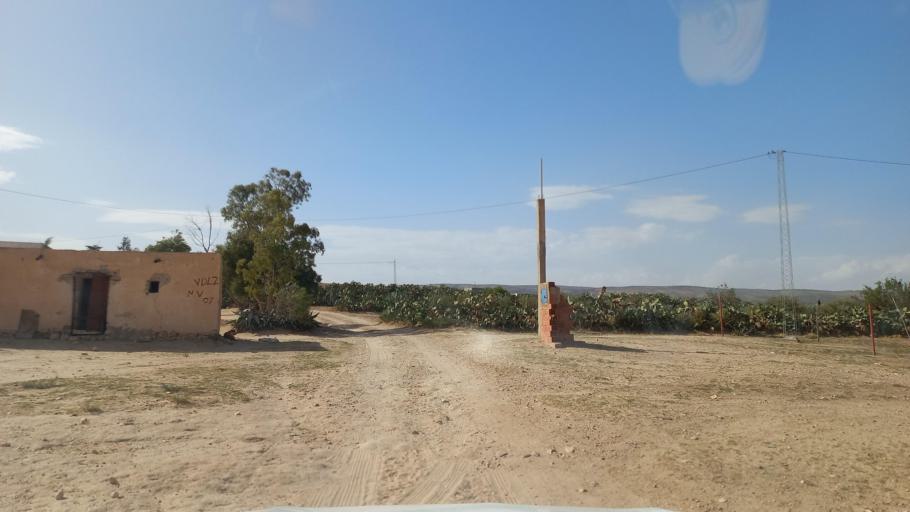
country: TN
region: Al Qasrayn
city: Kasserine
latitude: 35.2797
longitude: 8.9443
